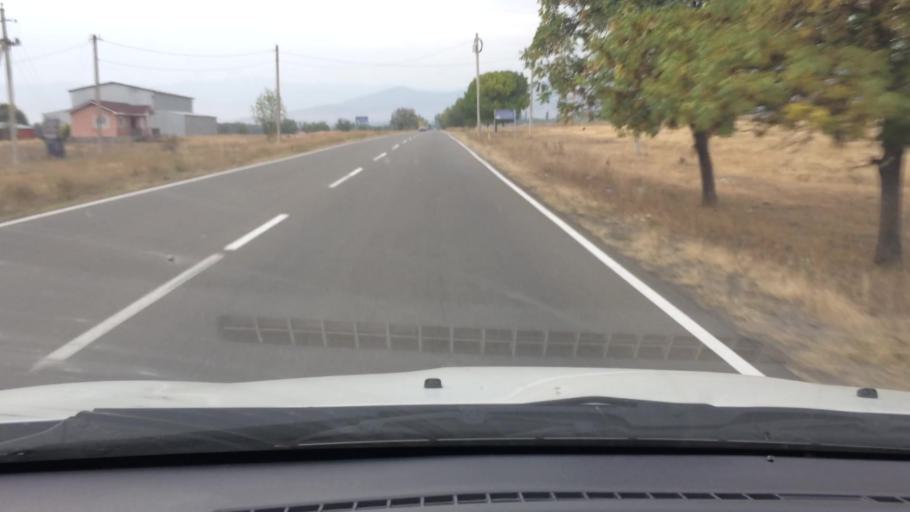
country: GE
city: Naghvarevi
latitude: 41.3398
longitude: 44.8113
